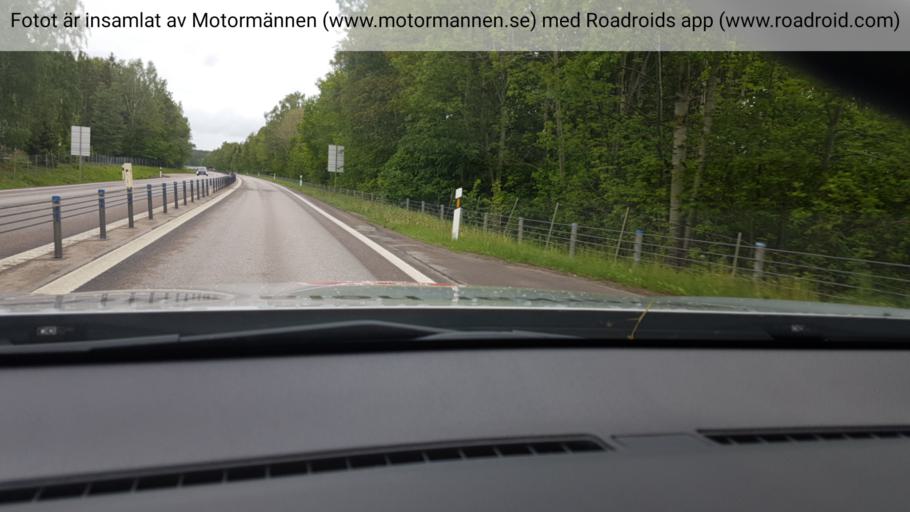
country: SE
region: Vaestra Goetaland
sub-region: Skovde Kommun
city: Stopen
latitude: 58.4902
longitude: 13.8504
